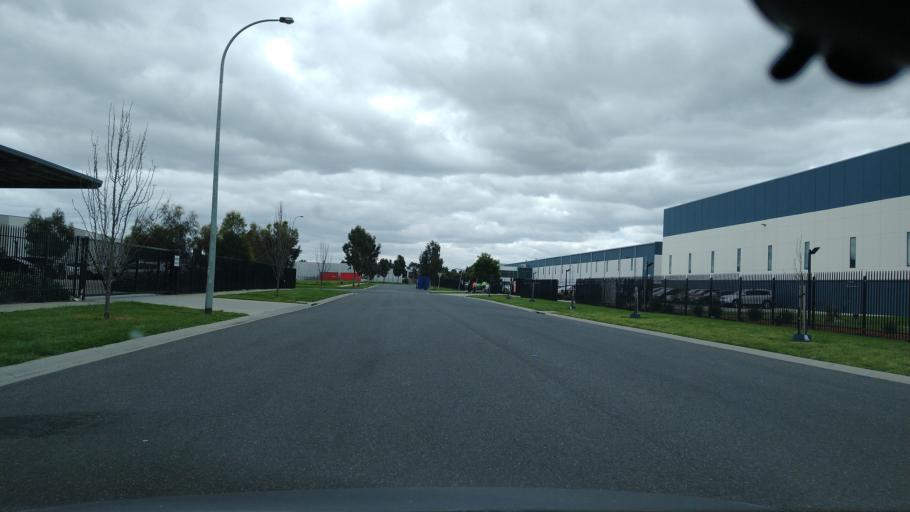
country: AU
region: Victoria
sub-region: Frankston
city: Sandhurst
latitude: -38.0527
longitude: 145.2133
